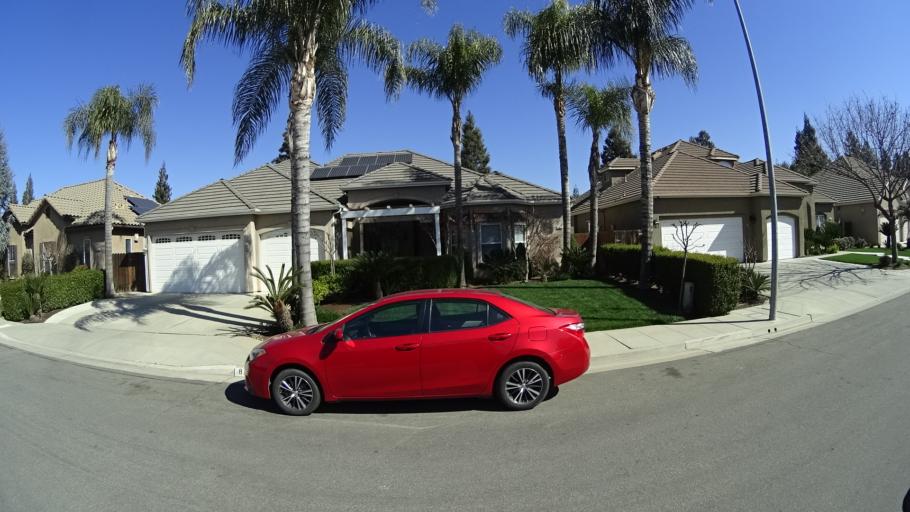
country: US
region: California
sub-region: Fresno County
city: Clovis
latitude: 36.8622
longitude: -119.7462
